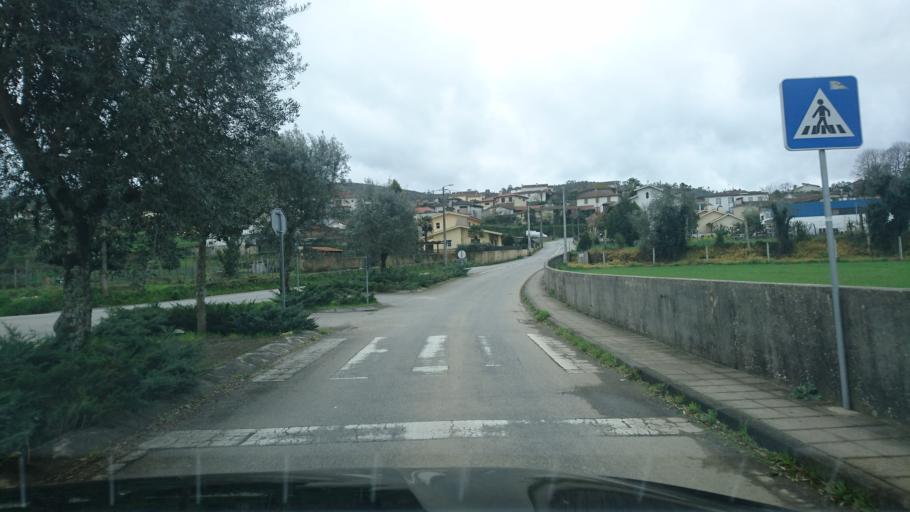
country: PT
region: Porto
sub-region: Paredes
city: Recarei
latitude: 41.1422
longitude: -8.3914
